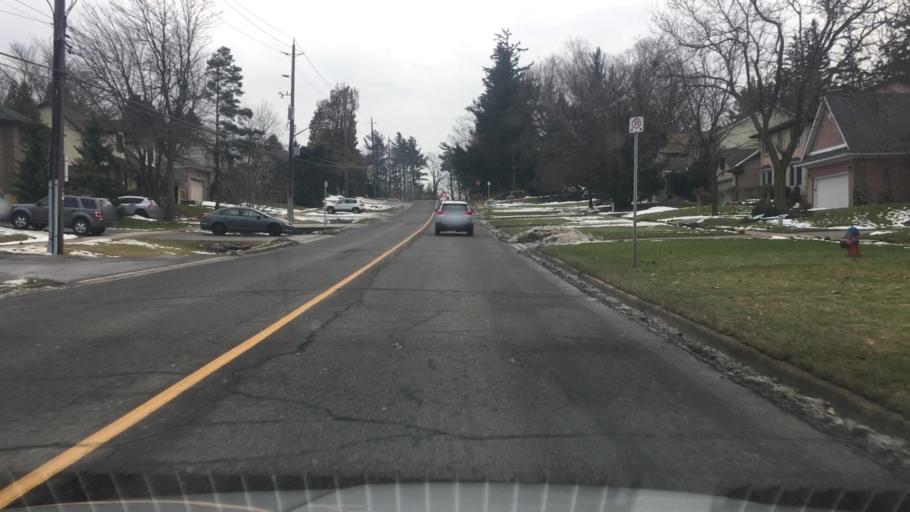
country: CA
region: Ontario
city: Ancaster
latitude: 43.2264
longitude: -79.9633
